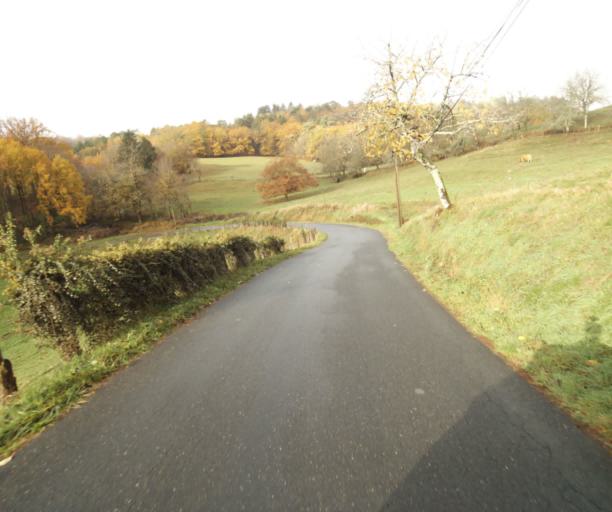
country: FR
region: Limousin
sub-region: Departement de la Correze
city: Cornil
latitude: 45.2042
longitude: 1.6523
